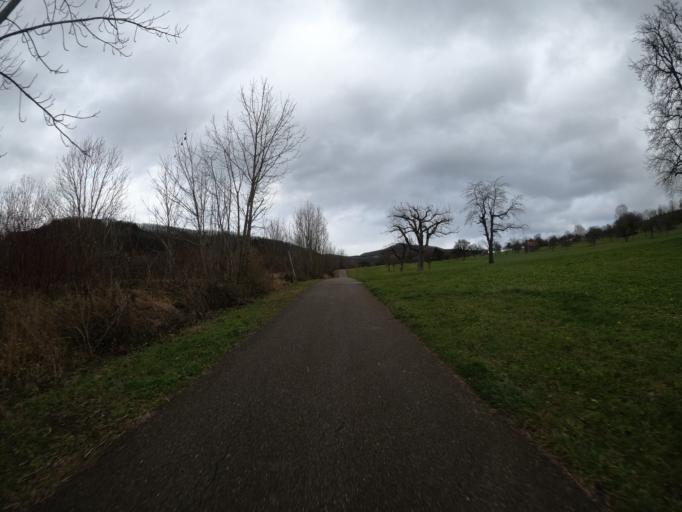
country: DE
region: Baden-Wuerttemberg
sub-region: Regierungsbezirk Stuttgart
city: Donzdorf
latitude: 48.6927
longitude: 9.8179
